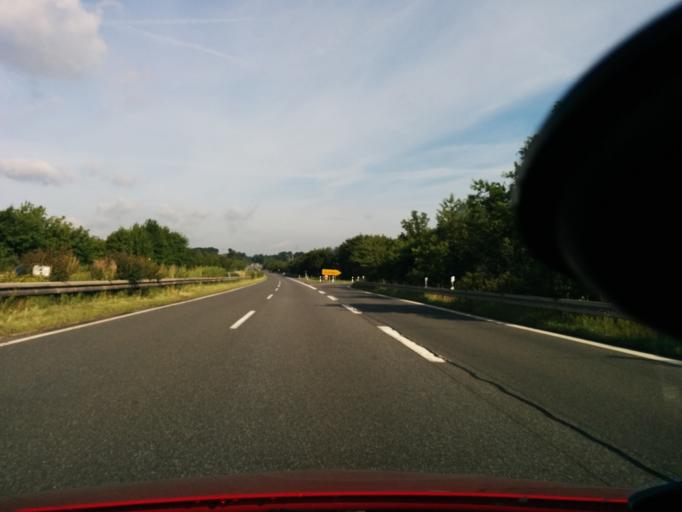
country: DE
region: Lower Saxony
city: Vienenburg
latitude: 51.9247
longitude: 10.5094
